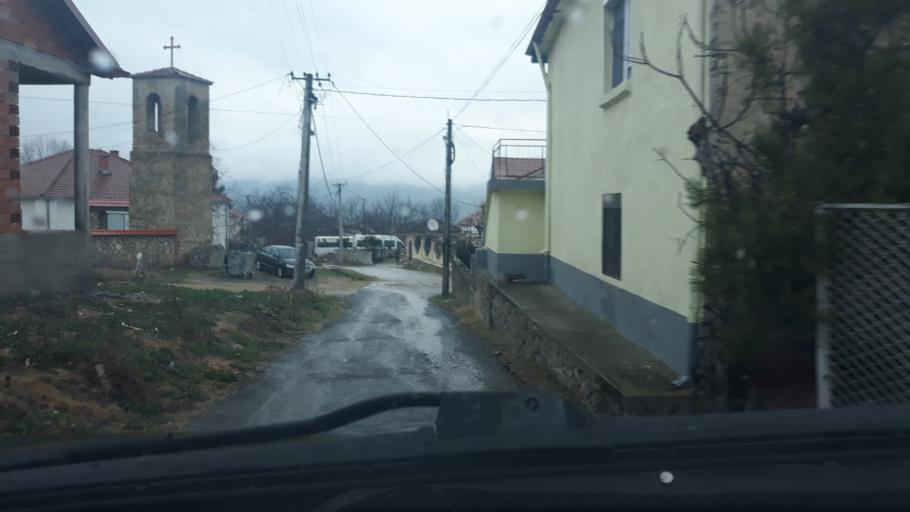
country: MK
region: Bogdanci
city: Bogdanci
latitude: 41.2399
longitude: 22.6126
